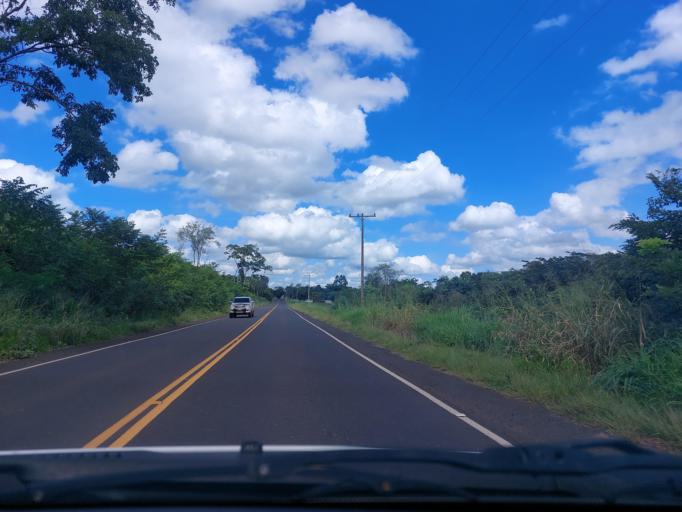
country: PY
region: San Pedro
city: Guayaybi
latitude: -24.5624
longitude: -56.5196
